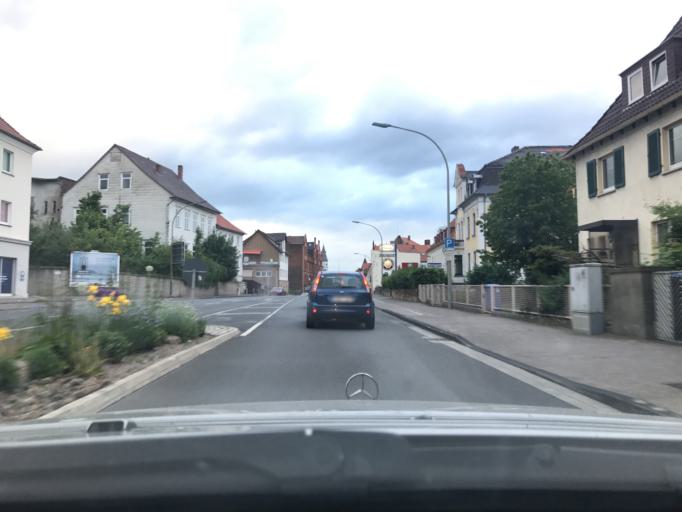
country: DE
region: Hesse
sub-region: Regierungsbezirk Kassel
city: Eschwege
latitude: 51.1864
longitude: 10.0483
